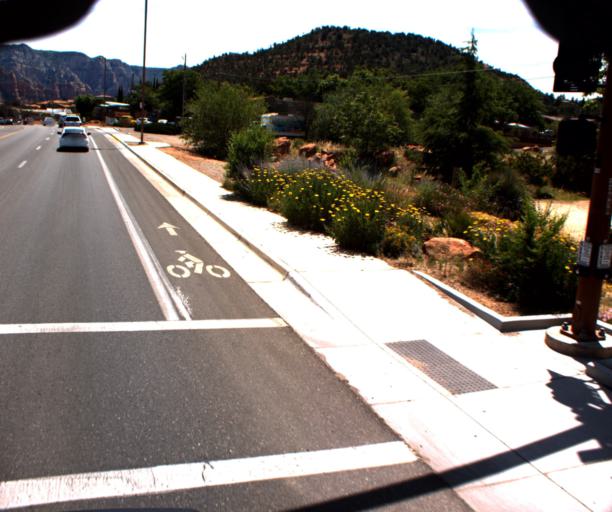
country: US
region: Arizona
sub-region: Yavapai County
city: West Sedona
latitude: 34.8626
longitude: -111.7832
